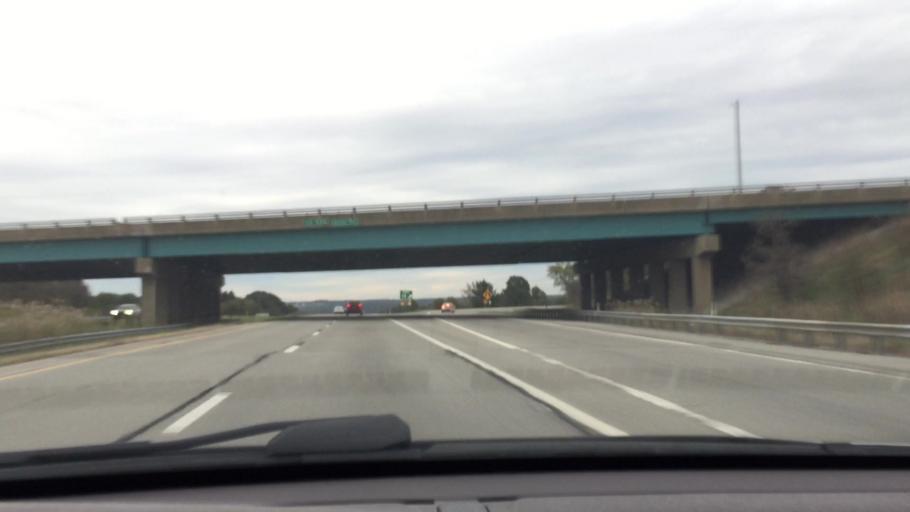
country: US
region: Pennsylvania
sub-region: Lawrence County
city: Oakwood
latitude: 41.0103
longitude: -80.3910
